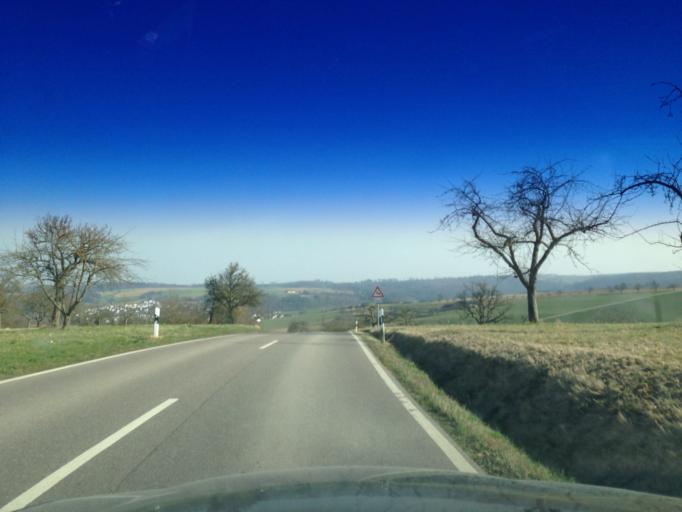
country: DE
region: Baden-Wuerttemberg
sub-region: Regierungsbezirk Stuttgart
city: Eberdingen
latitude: 48.8858
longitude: 8.9461
